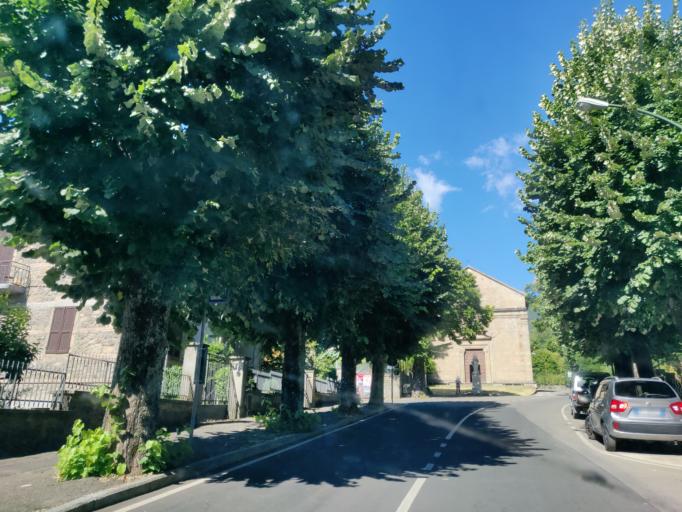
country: IT
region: Tuscany
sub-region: Provincia di Siena
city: Abbadia San Salvatore
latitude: 42.8821
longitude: 11.6697
